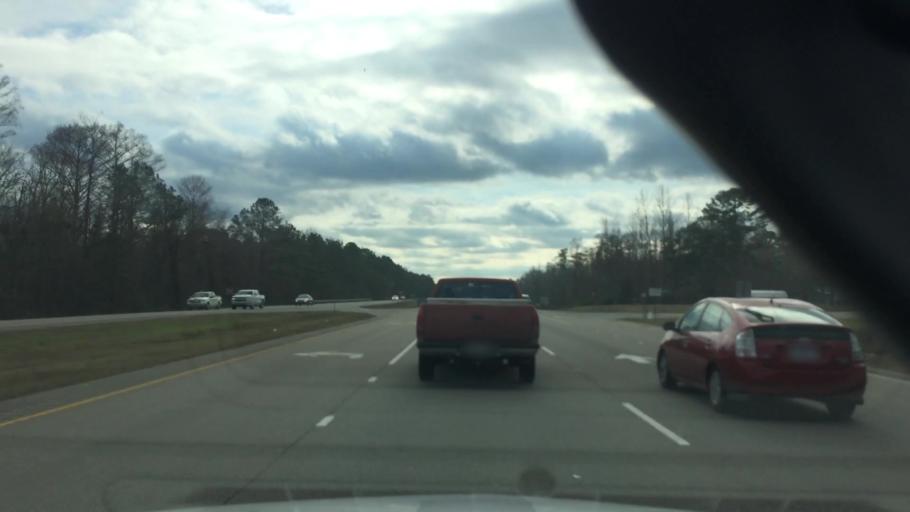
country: US
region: North Carolina
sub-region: Brunswick County
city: Leland
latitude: 34.1607
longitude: -78.0910
